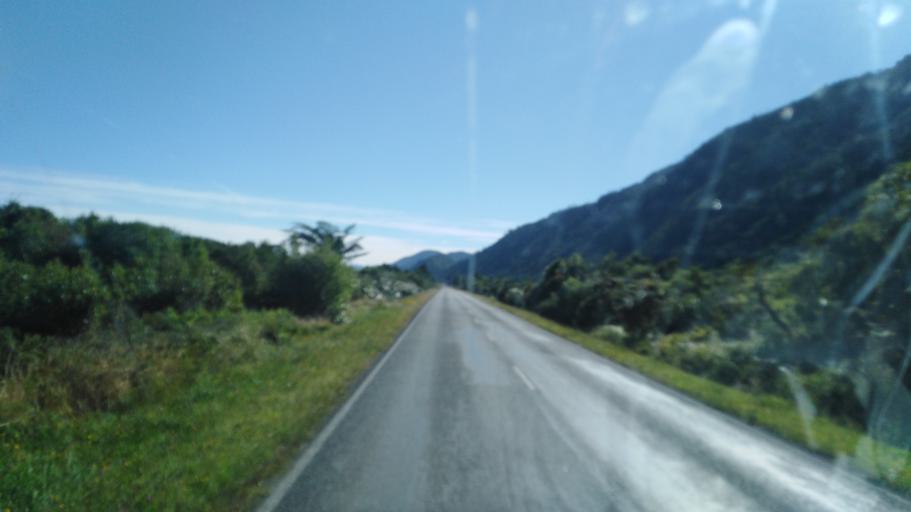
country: NZ
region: West Coast
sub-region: Buller District
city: Westport
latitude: -41.6487
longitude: 171.8337
